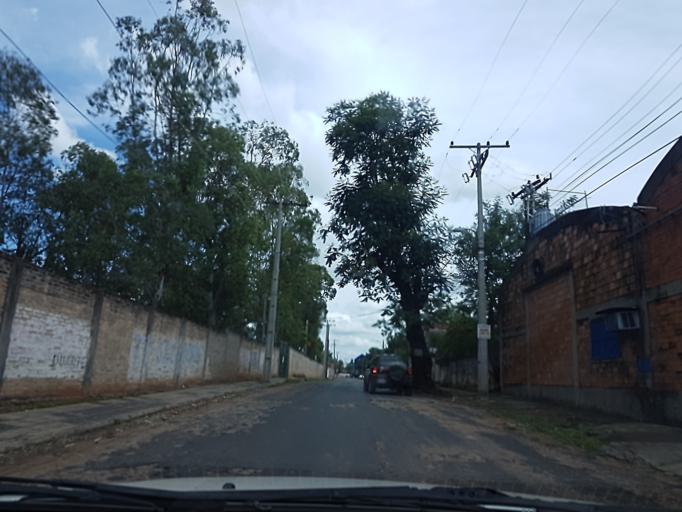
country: PY
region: Central
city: Colonia Mariano Roque Alonso
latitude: -25.2294
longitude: -57.5312
